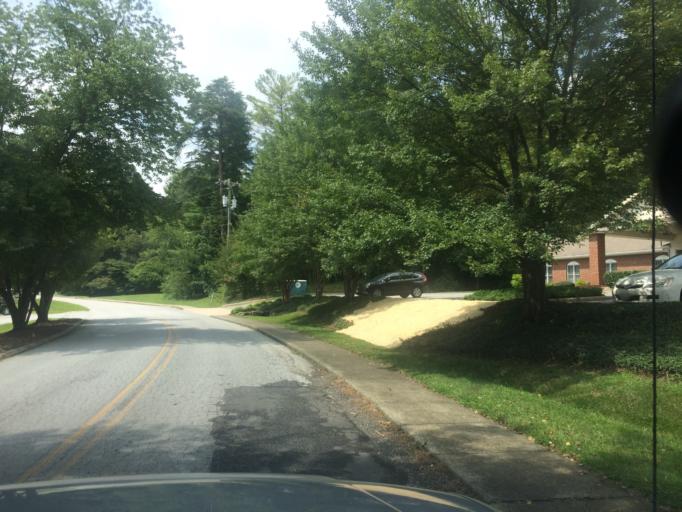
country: US
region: North Carolina
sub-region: Henderson County
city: Laurel Park
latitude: 35.3225
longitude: -82.4904
